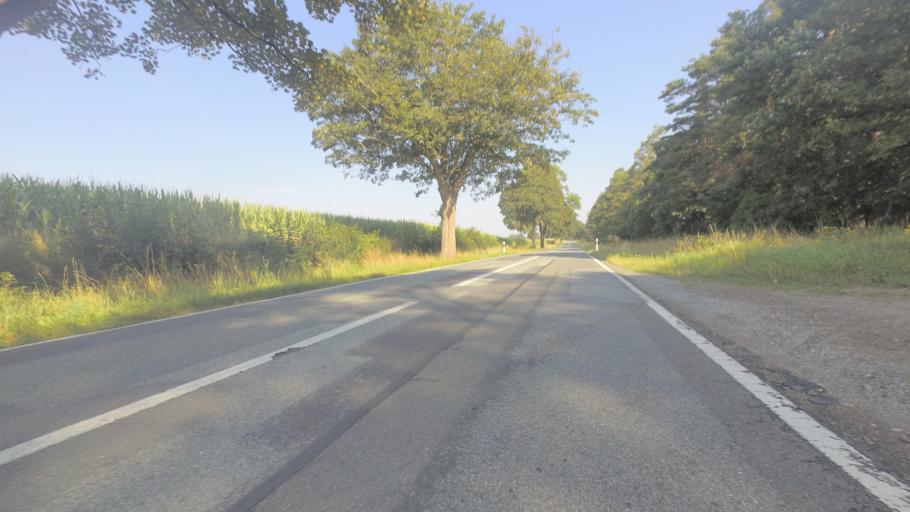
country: DE
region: Mecklenburg-Vorpommern
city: Grabowhofe
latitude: 53.6017
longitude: 12.4697
